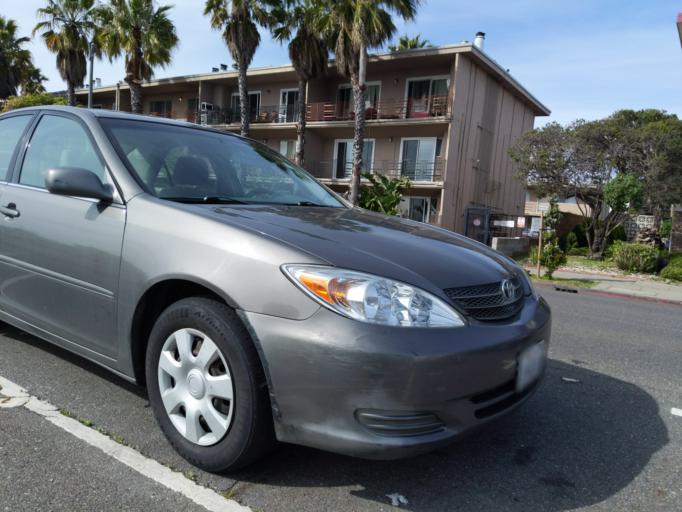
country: US
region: California
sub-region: Alameda County
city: Alameda
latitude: 37.7580
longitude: -122.2602
